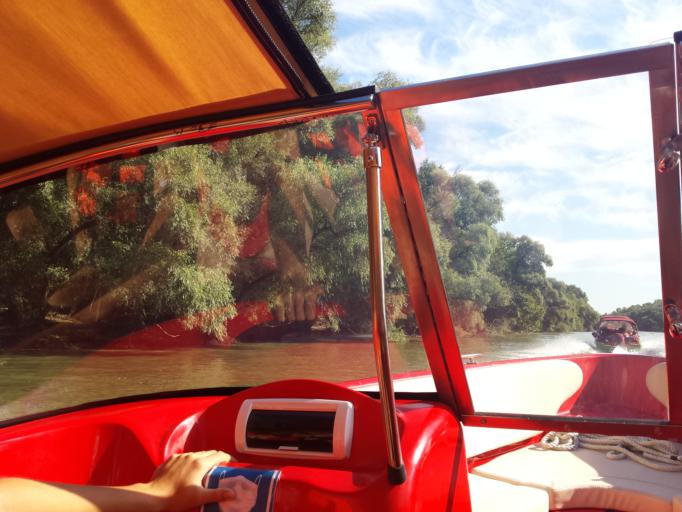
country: RO
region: Tulcea
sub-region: Comuna Nufaru
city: Nufaru
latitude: 45.2191
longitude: 28.8762
